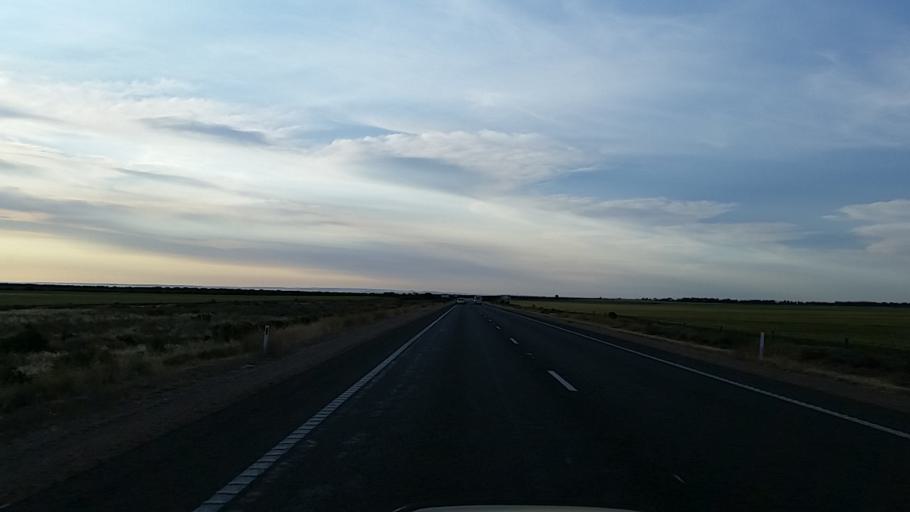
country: AU
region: South Australia
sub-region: Port Pirie City and Dists
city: Port Pirie
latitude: -33.0946
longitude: 138.0596
